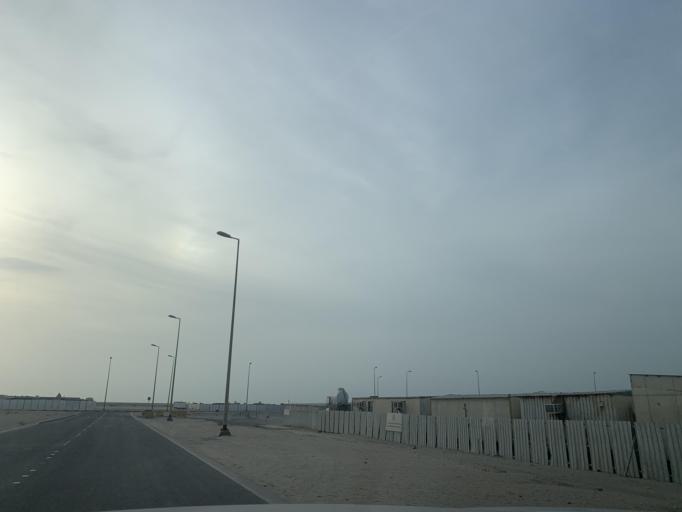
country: BH
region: Muharraq
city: Al Muharraq
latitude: 26.3109
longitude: 50.6201
